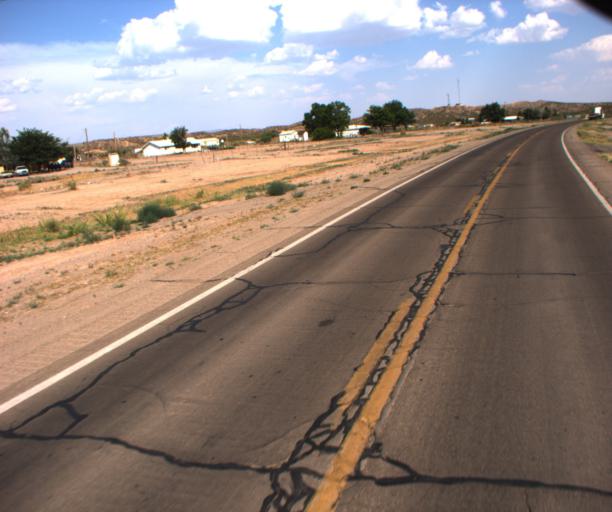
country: US
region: Arizona
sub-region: Greenlee County
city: Clifton
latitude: 32.7405
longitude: -109.0960
